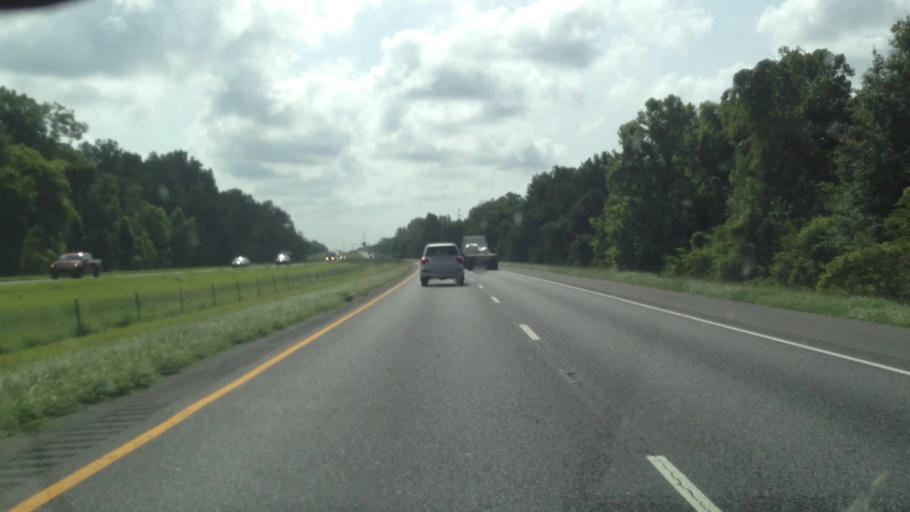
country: US
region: Louisiana
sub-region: Ascension Parish
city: Sorrento
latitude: 30.1559
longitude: -90.8202
